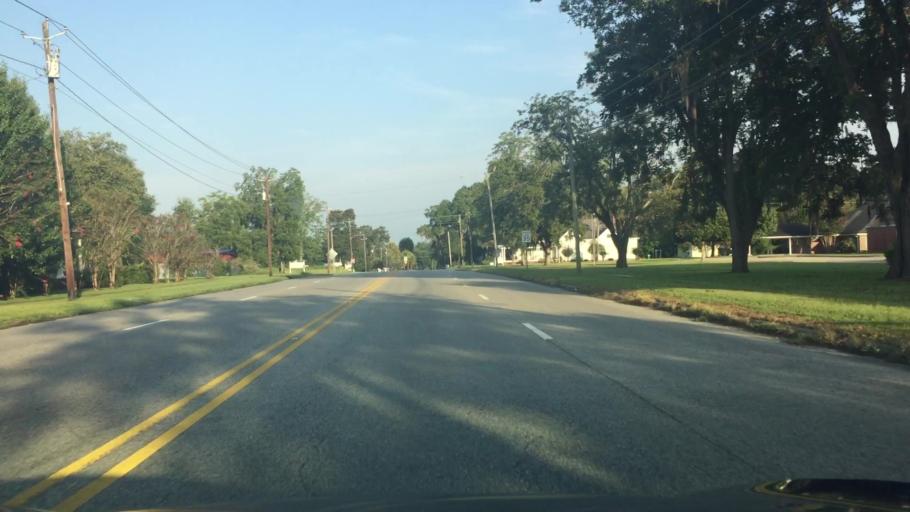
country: US
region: Alabama
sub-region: Covington County
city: Florala
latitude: 30.9997
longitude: -86.3124
